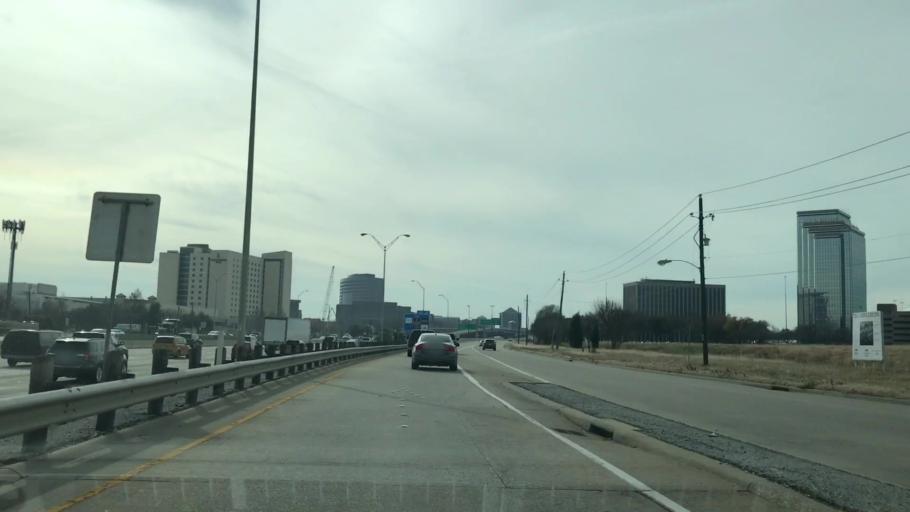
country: US
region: Texas
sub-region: Collin County
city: Plano
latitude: 32.9900
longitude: -96.7105
